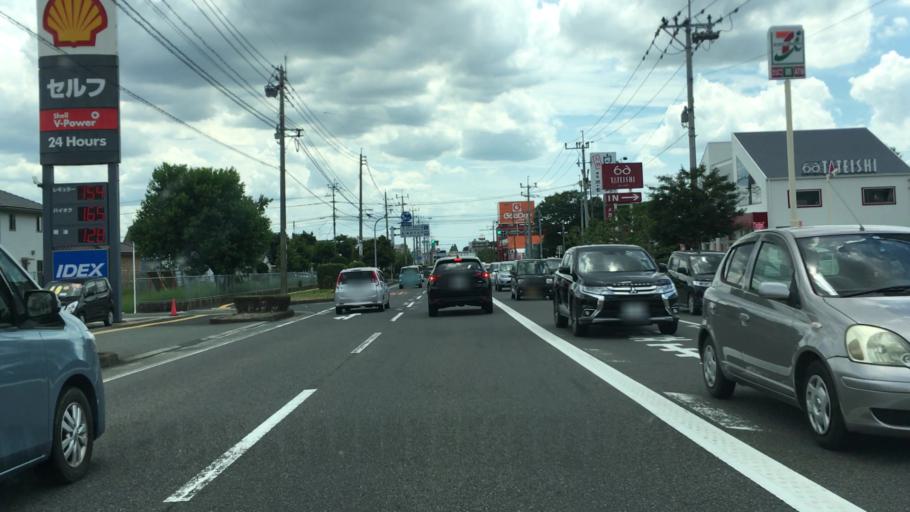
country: JP
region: Saga Prefecture
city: Tosu
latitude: 33.3790
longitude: 130.4990
